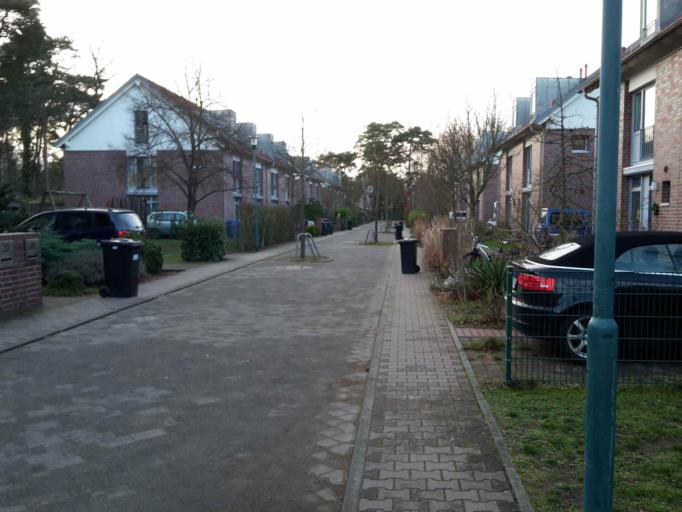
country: DE
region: Brandenburg
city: Kleinmachnow
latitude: 52.4121
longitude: 13.2386
